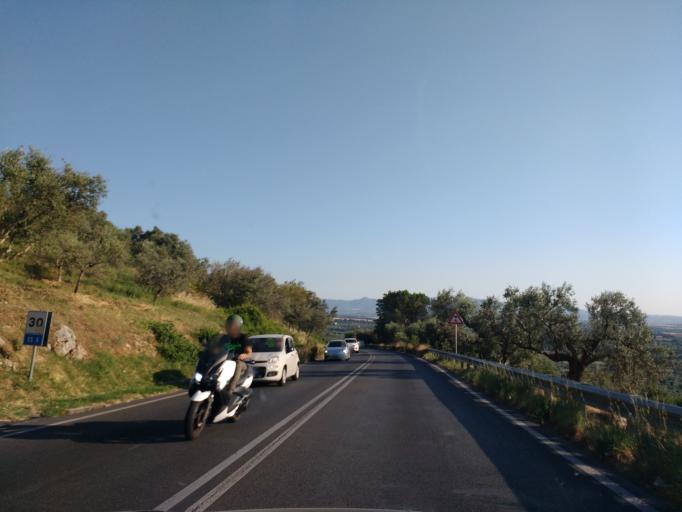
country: IT
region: Latium
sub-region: Citta metropolitana di Roma Capitale
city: Tivoli
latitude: 41.9524
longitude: 12.7911
